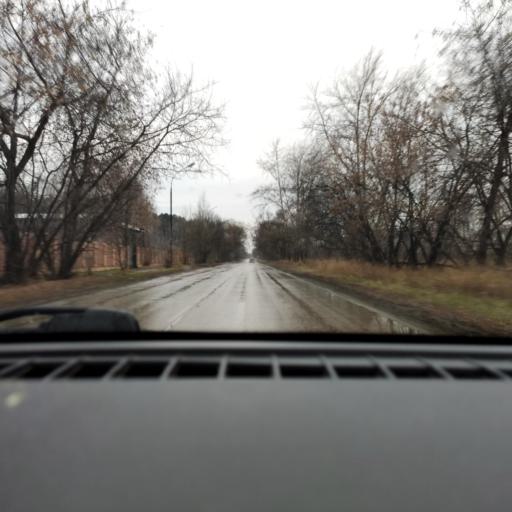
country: RU
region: Perm
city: Kultayevo
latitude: 57.9935
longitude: 55.9186
